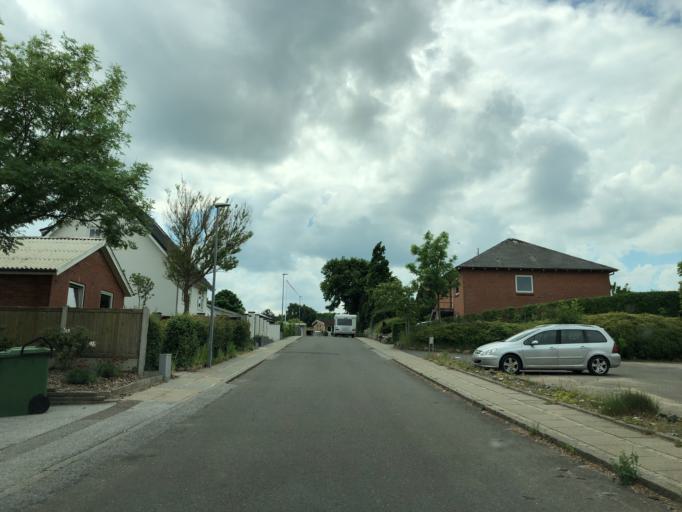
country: DK
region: Central Jutland
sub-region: Struer Kommune
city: Struer
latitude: 56.4907
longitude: 8.5770
